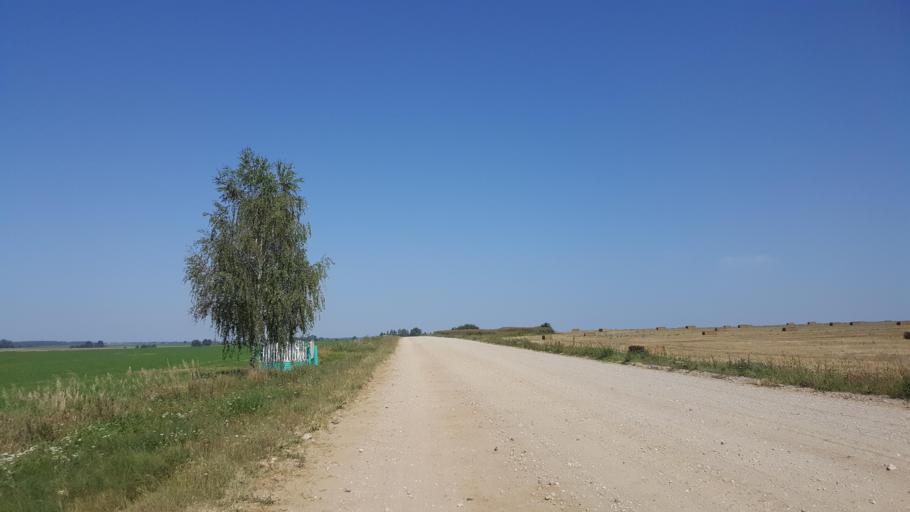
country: BY
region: Brest
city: Vysokaye
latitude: 52.4516
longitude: 23.4447
